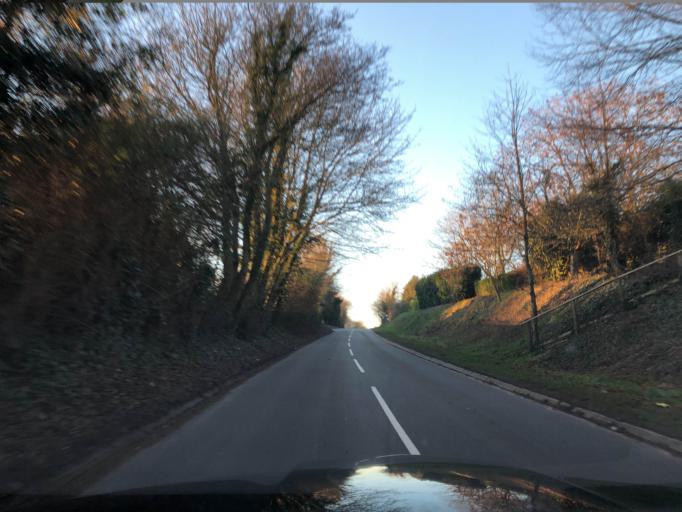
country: GB
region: England
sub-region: Warwickshire
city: Harbury
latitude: 52.2156
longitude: -1.4369
